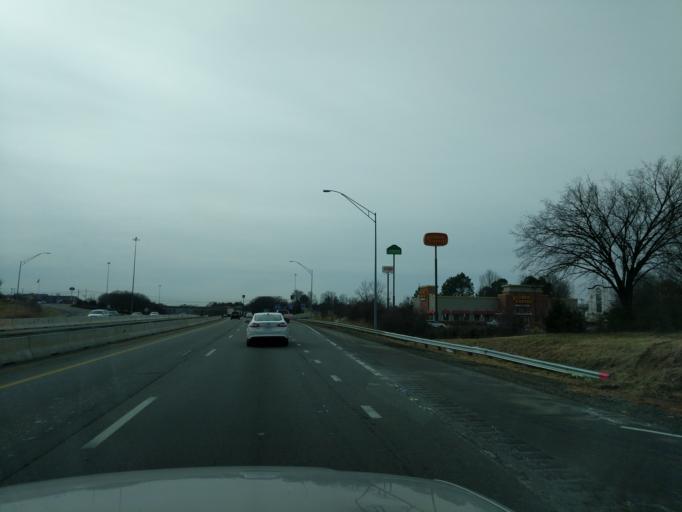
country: US
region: North Carolina
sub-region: Iredell County
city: Mooresville
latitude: 35.5976
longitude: -80.8603
